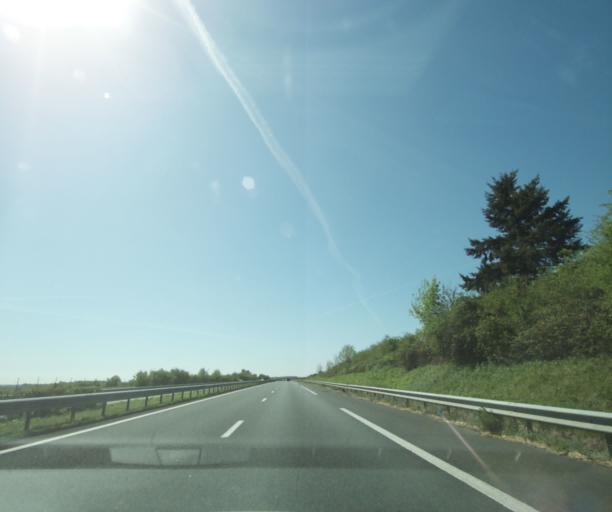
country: FR
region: Centre
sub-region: Departement de l'Indre
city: Luant
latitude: 46.6812
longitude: 1.5794
